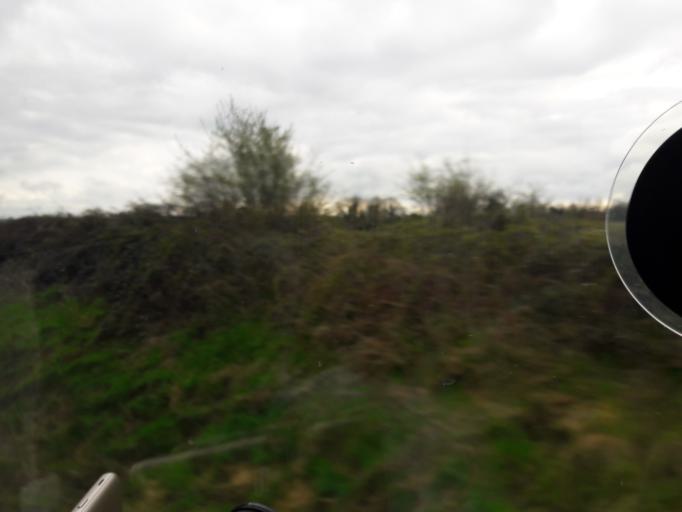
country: IE
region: Leinster
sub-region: An Longfort
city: Granard
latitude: 53.6727
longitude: -7.5156
